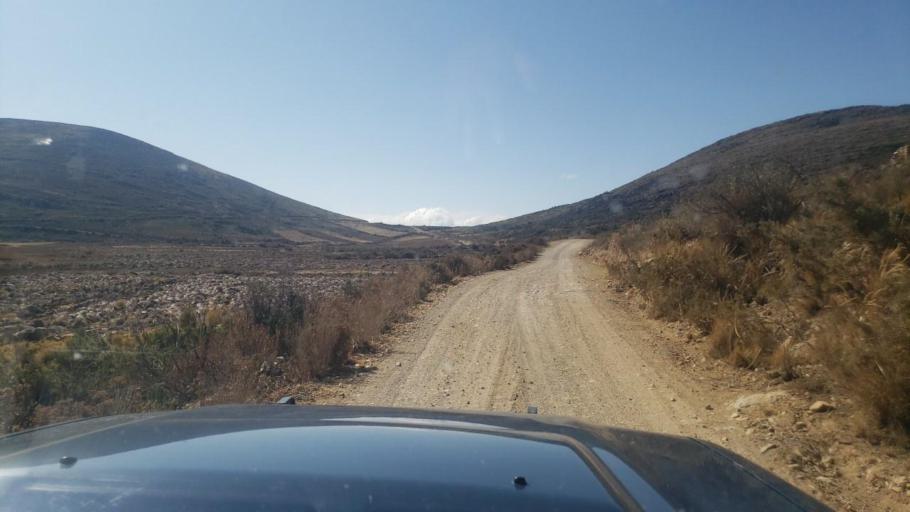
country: BO
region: La Paz
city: Huatajata
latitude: -16.3337
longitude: -68.6923
